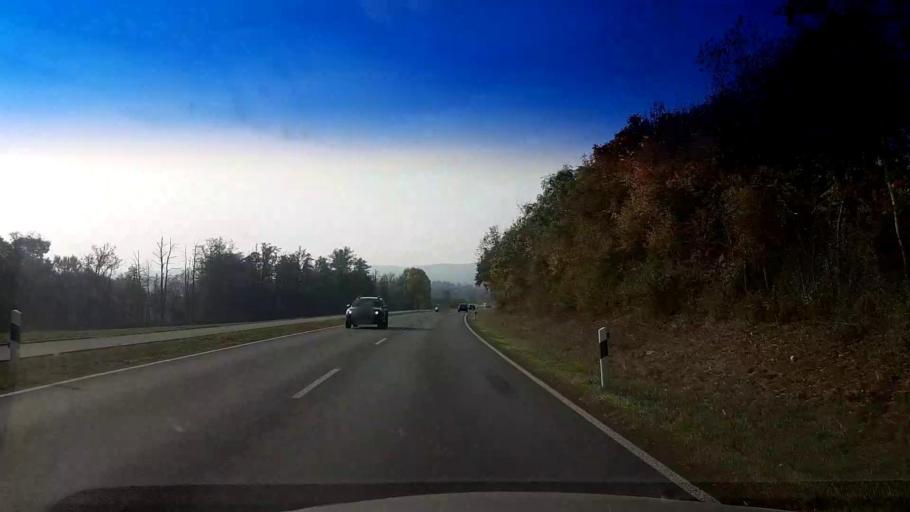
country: DE
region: Bavaria
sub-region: Upper Franconia
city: Himmelkron
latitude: 50.0726
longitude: 11.6087
